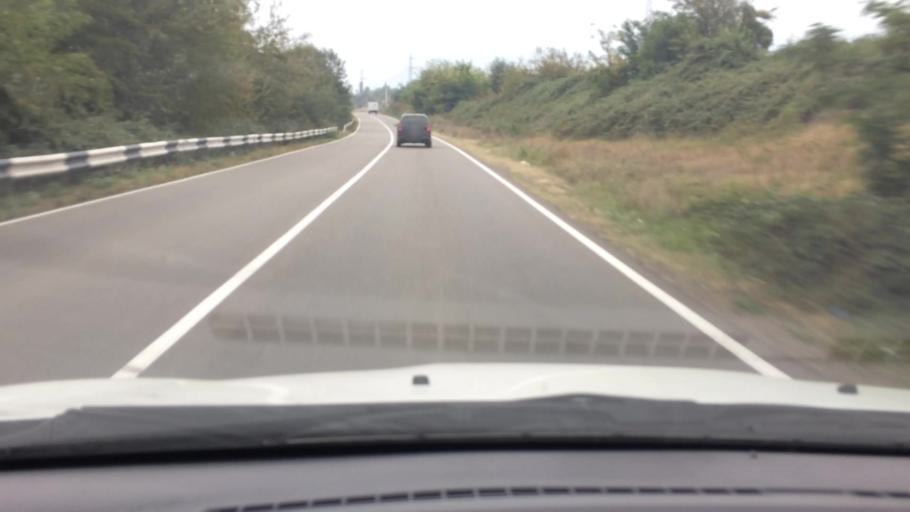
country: AM
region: Tavush
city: Bagratashen
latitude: 41.2707
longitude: 44.7907
